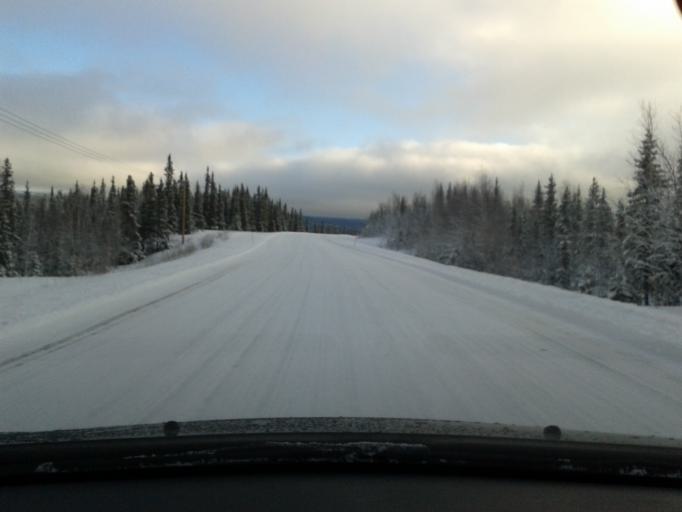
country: SE
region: Vaesterbotten
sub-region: Vilhelmina Kommun
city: Sjoberg
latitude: 65.2569
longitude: 15.6572
